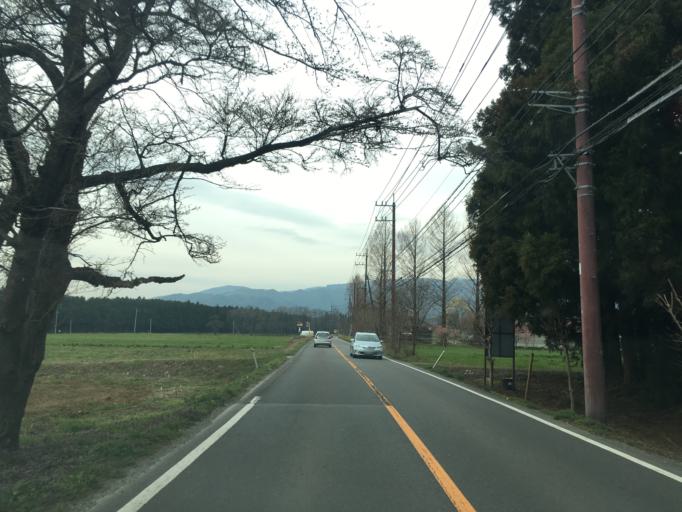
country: JP
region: Tochigi
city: Kuroiso
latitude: 36.9629
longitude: 139.9133
